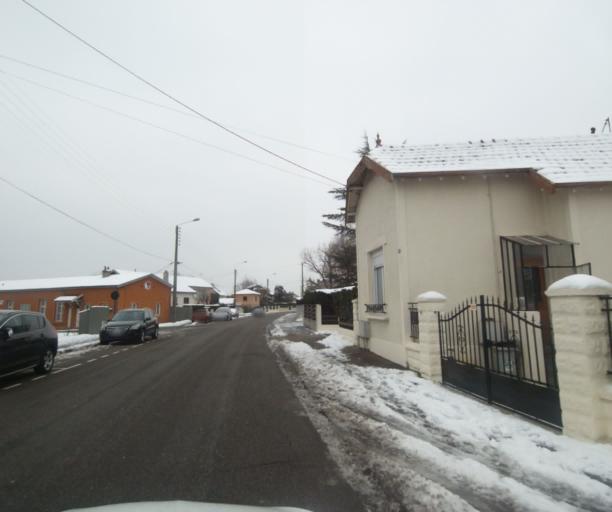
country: FR
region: Champagne-Ardenne
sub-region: Departement de la Haute-Marne
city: Saint-Dizier
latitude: 48.6331
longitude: 4.9358
